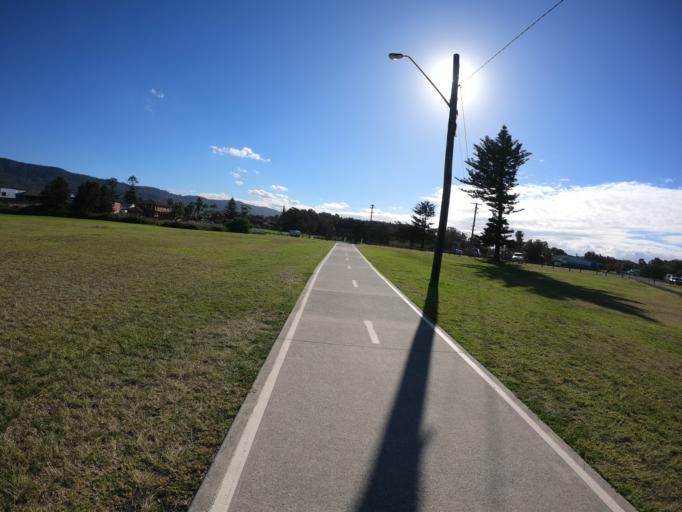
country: AU
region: New South Wales
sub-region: Wollongong
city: East Corrimal
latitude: -34.3819
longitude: 150.9145
